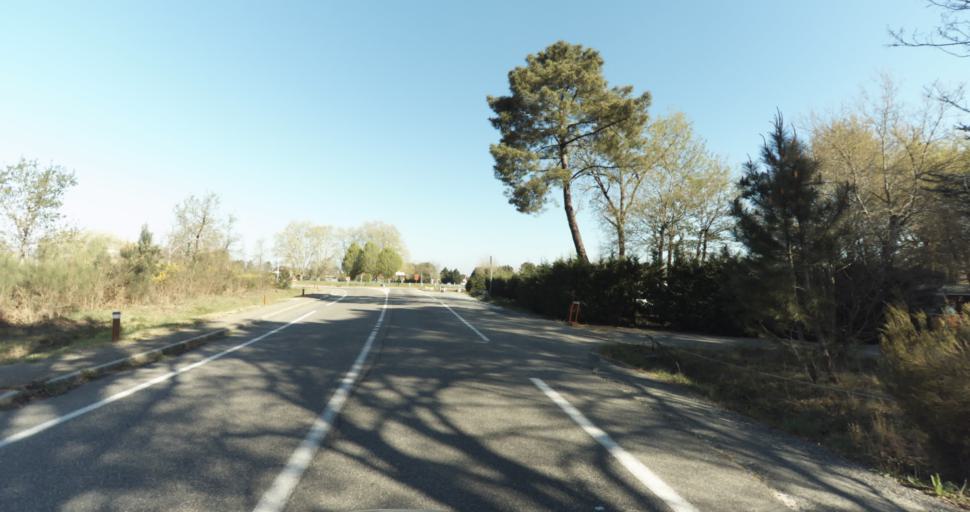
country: FR
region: Aquitaine
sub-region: Departement de la Gironde
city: Marcheprime
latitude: 44.7820
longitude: -0.9330
